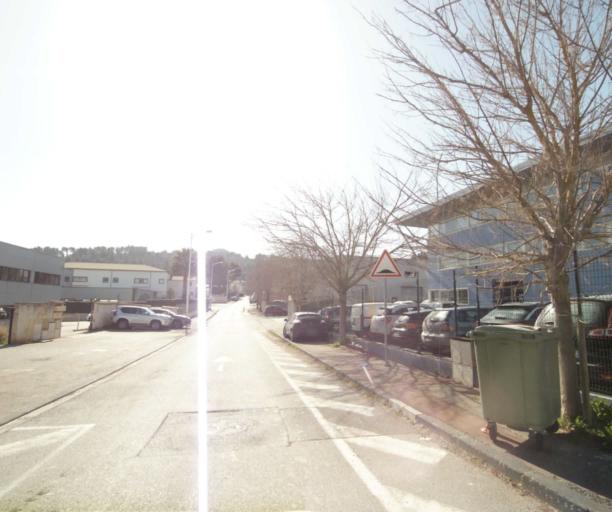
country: FR
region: Provence-Alpes-Cote d'Azur
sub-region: Departement des Bouches-du-Rhone
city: Gardanne
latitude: 43.4483
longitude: 5.4540
